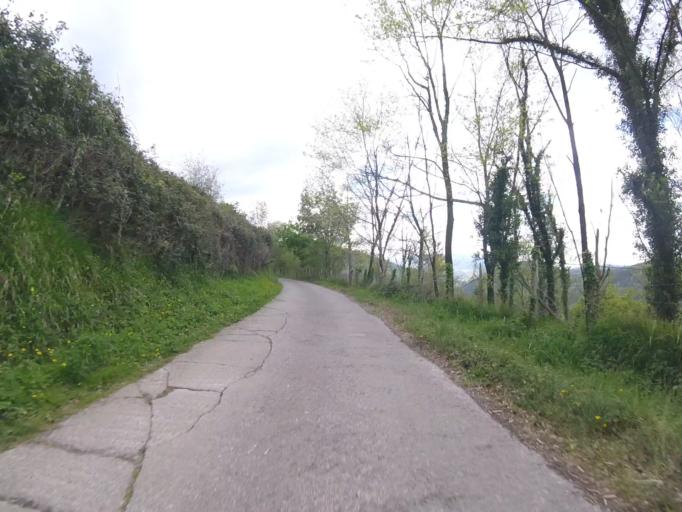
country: ES
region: Basque Country
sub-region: Provincia de Guipuzcoa
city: Aizarnazabal
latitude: 43.2536
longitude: -2.2146
